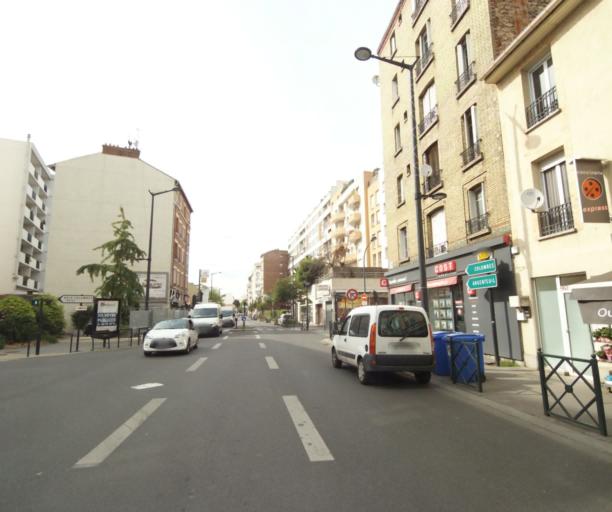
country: FR
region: Ile-de-France
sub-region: Departement des Hauts-de-Seine
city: Bois-Colombes
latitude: 48.9211
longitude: 2.2785
